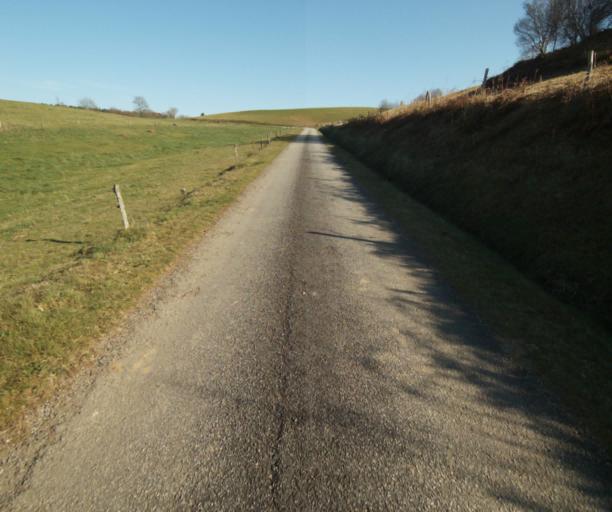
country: FR
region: Limousin
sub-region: Departement de la Correze
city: Chamboulive
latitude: 45.4880
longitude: 1.7292
